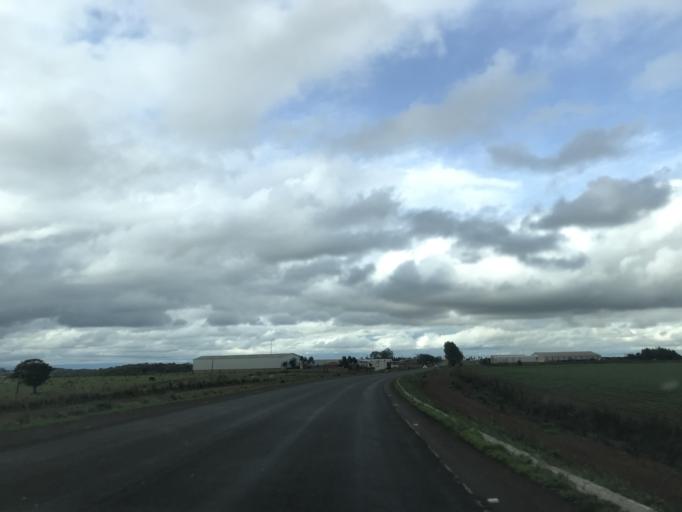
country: BR
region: Goias
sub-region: Vianopolis
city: Vianopolis
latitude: -16.7727
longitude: -48.5232
